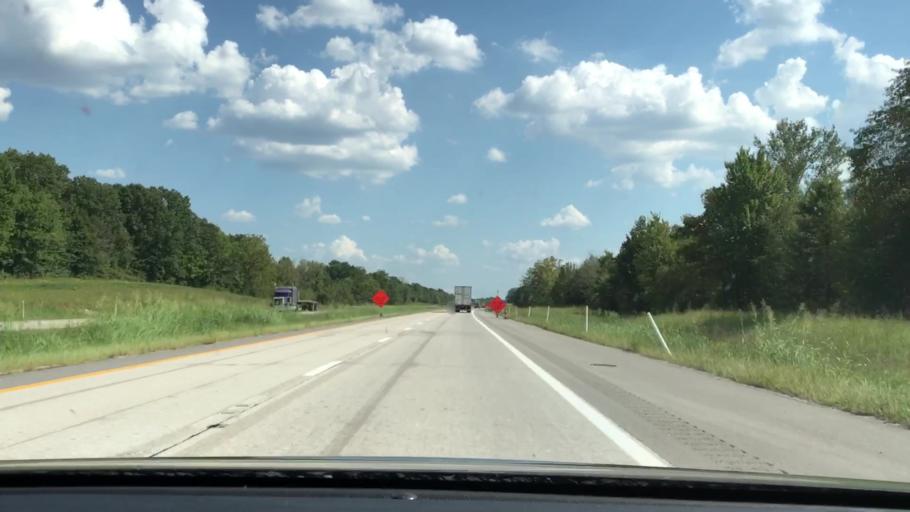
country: US
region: Kentucky
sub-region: Ohio County
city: Oak Grove
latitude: 37.3440
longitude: -86.7734
